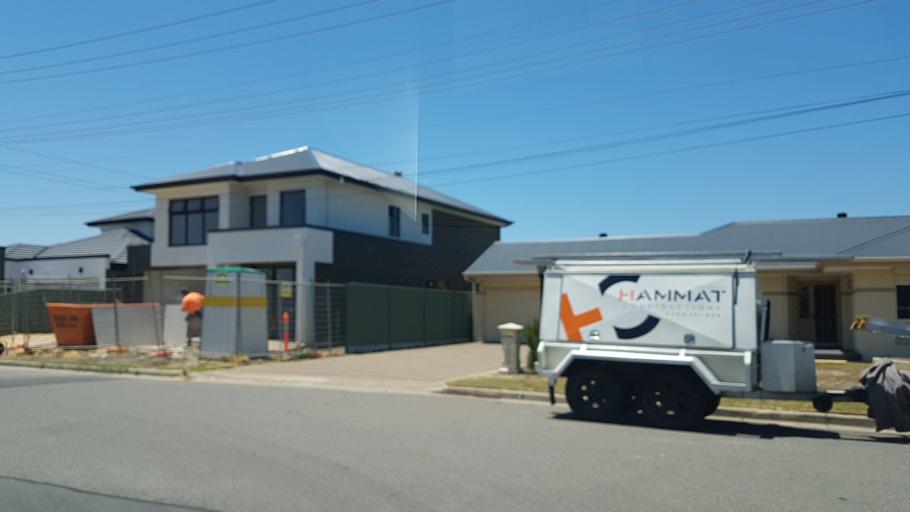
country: AU
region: South Australia
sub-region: Charles Sturt
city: West Lakes Shore
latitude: -34.8575
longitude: 138.4853
